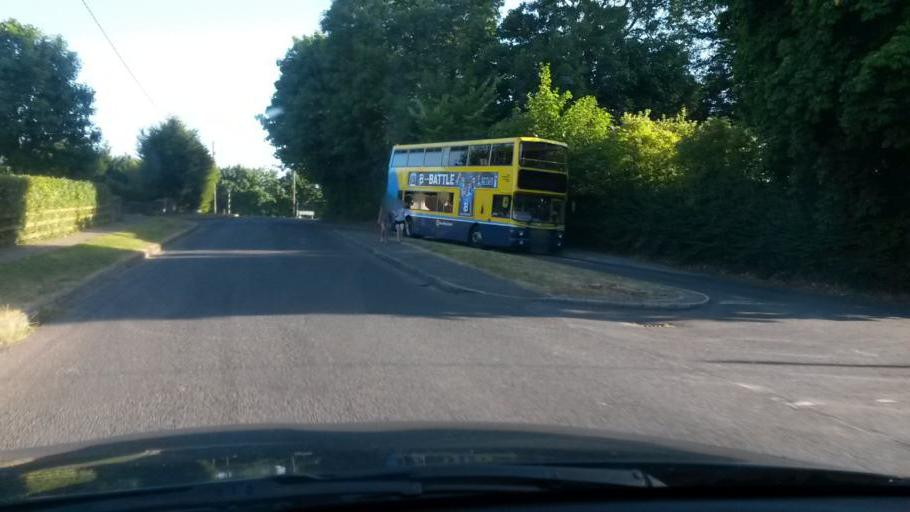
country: IE
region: Leinster
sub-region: Fingal County
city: Swords
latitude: 53.4890
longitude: -6.3040
